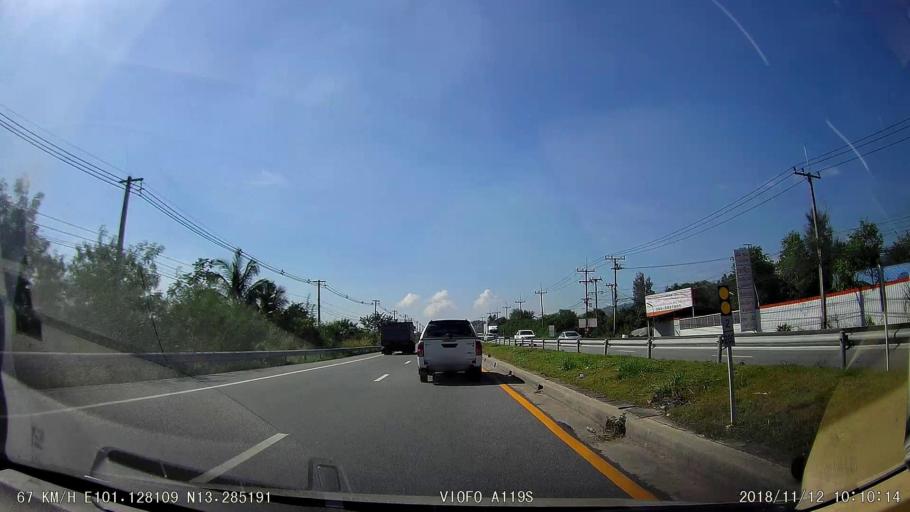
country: TH
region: Chon Buri
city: Ban Bueng
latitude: 13.2849
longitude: 101.1279
